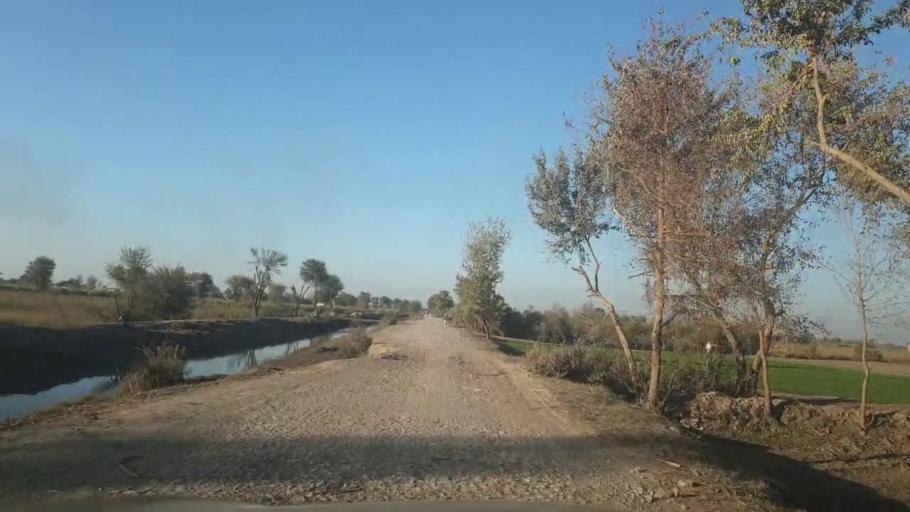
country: PK
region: Sindh
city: Ghotki
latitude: 27.9999
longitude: 69.2710
